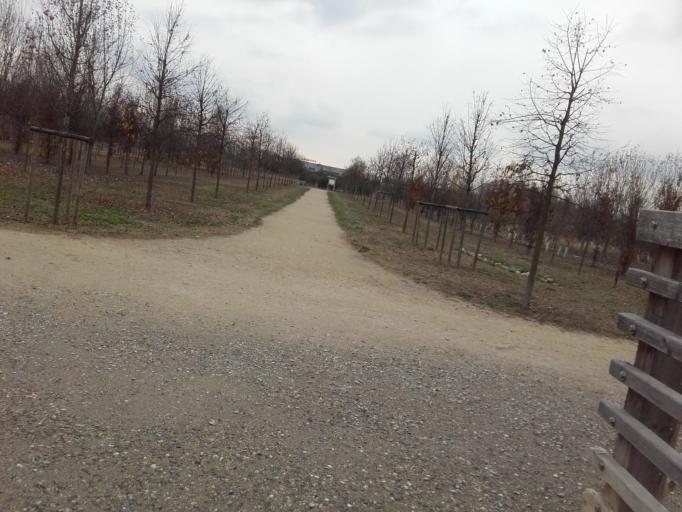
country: IT
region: Piedmont
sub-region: Provincia di Torino
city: Settimo Torinese
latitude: 45.1275
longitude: 7.7620
